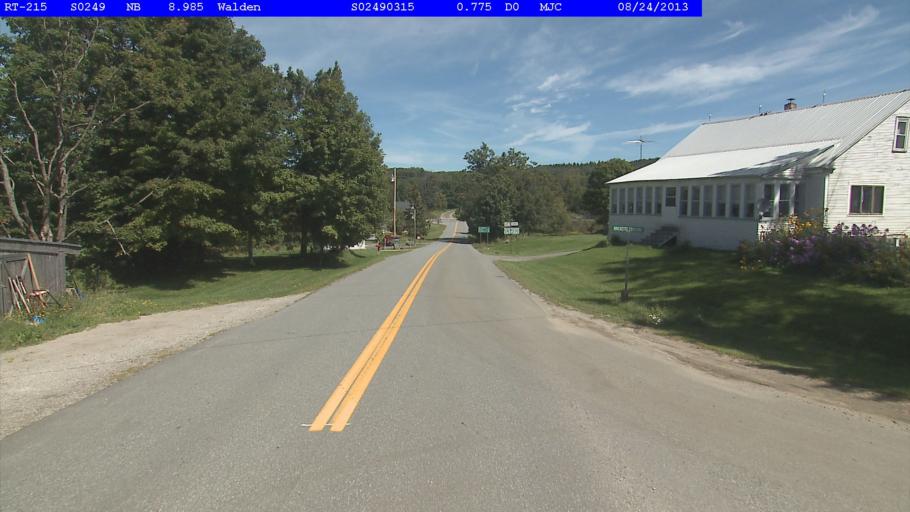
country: US
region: Vermont
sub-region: Caledonia County
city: Hardwick
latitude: 44.4502
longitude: -72.2583
